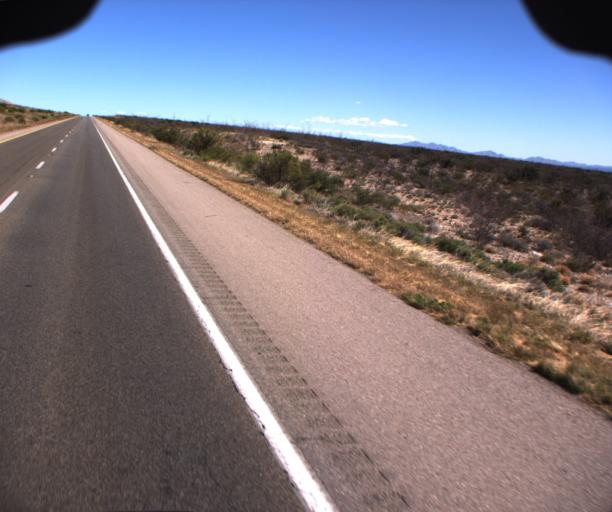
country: US
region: Arizona
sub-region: Cochise County
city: Huachuca City
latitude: 31.7639
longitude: -110.3500
